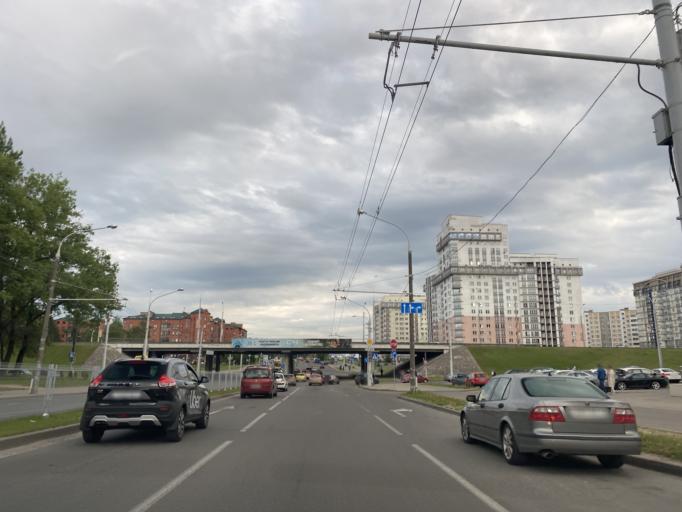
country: BY
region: Minsk
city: Lyeskawka
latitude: 53.9485
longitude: 27.6938
